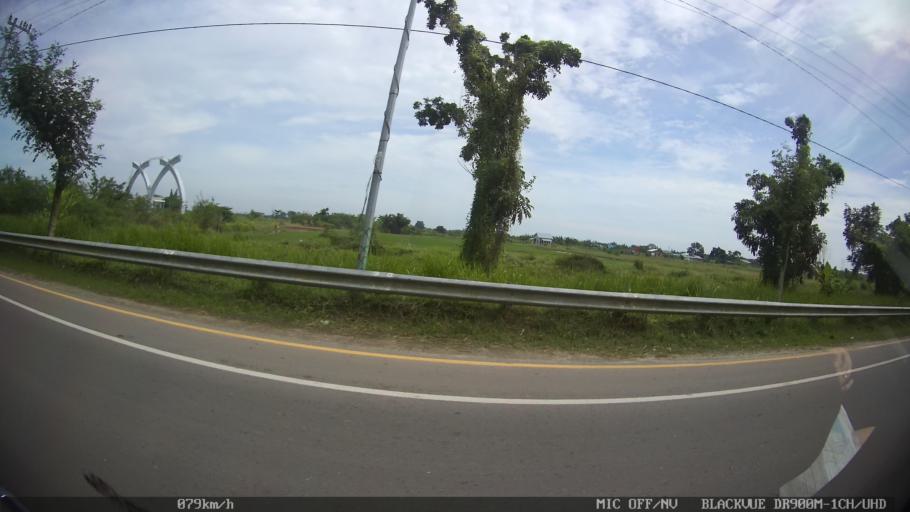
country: ID
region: North Sumatra
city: Percut
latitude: 3.5992
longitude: 98.8207
